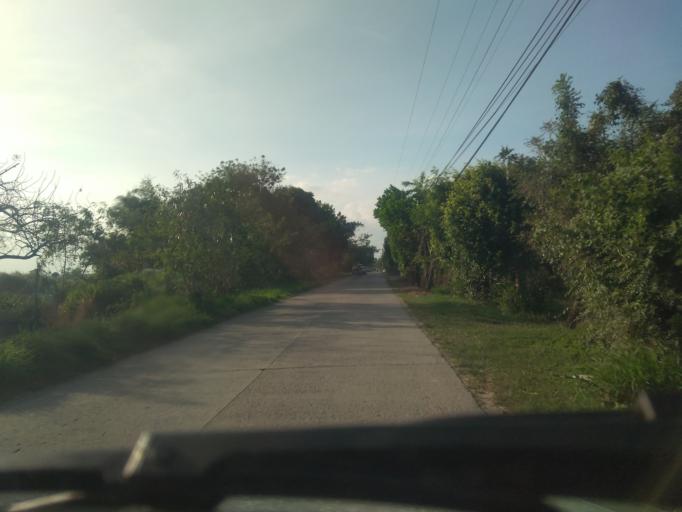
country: PH
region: Central Luzon
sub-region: Province of Pampanga
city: Mexico
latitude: 15.0850
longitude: 120.6971
